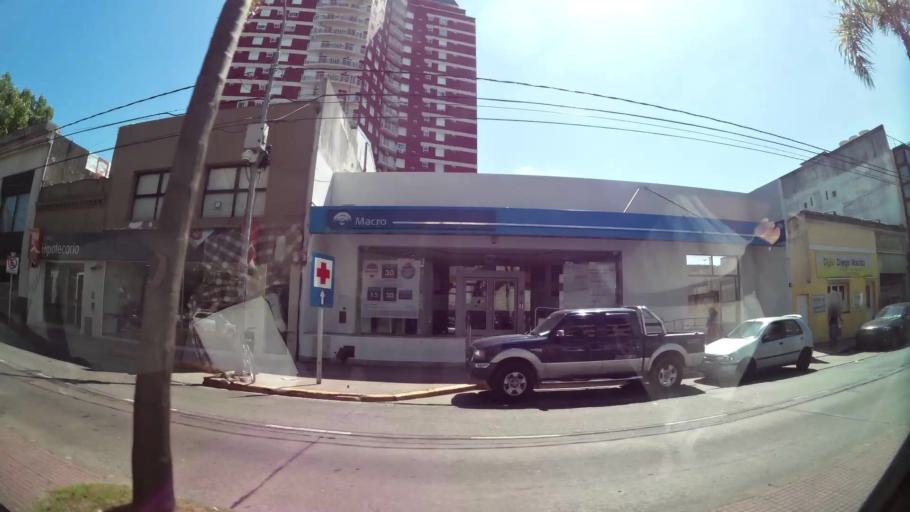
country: AR
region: Buenos Aires
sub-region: Partido de Tigre
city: Tigre
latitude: -34.4246
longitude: -58.5782
